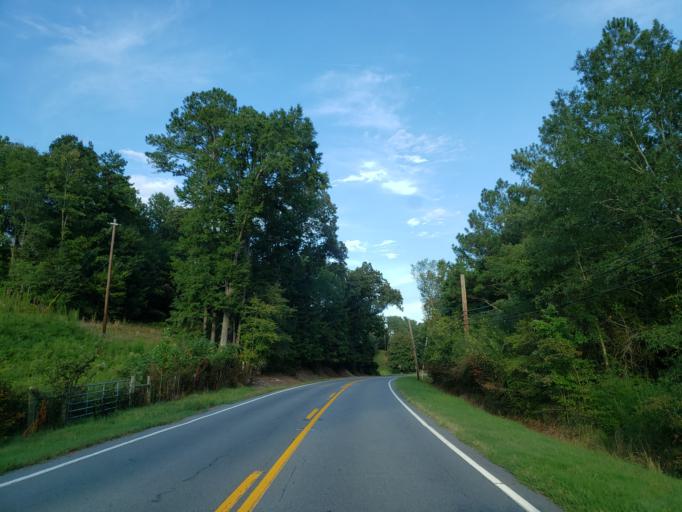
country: US
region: Georgia
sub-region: Bartow County
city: Euharlee
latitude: 34.2385
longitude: -84.9298
